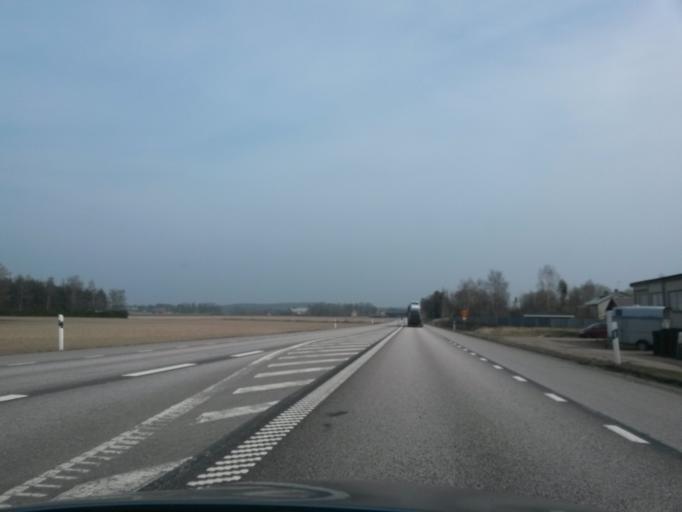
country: SE
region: Vaestra Goetaland
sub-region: Gullspangs Kommun
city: Hova
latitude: 58.8545
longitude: 14.2054
